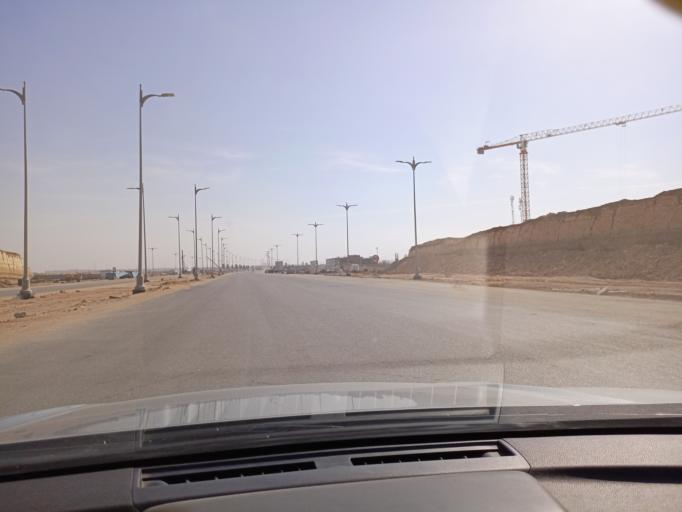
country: EG
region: Muhafazat al Qalyubiyah
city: Al Khankah
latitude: 30.0304
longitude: 31.6799
